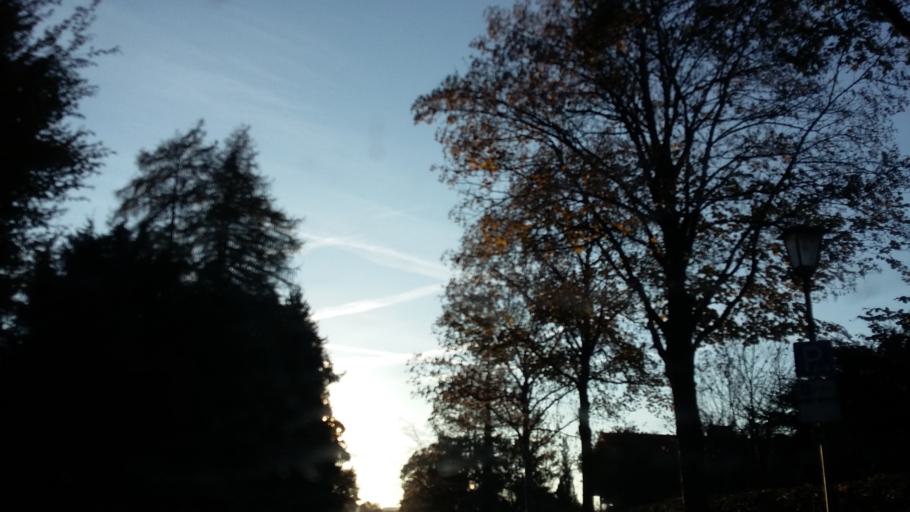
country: DE
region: Bavaria
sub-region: Upper Bavaria
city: Prien am Chiemsee
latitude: 47.8596
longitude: 12.3563
